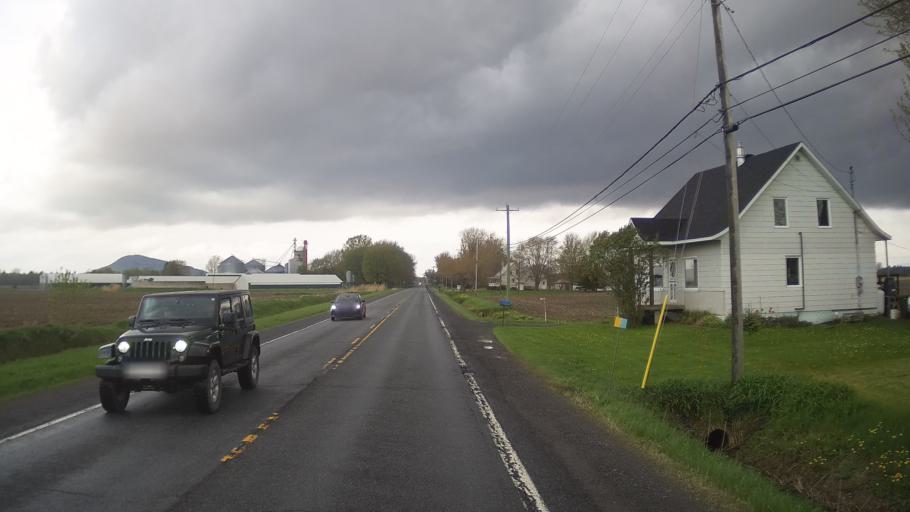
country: CA
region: Quebec
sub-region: Monteregie
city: Rougemont
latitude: 45.3368
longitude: -73.0845
